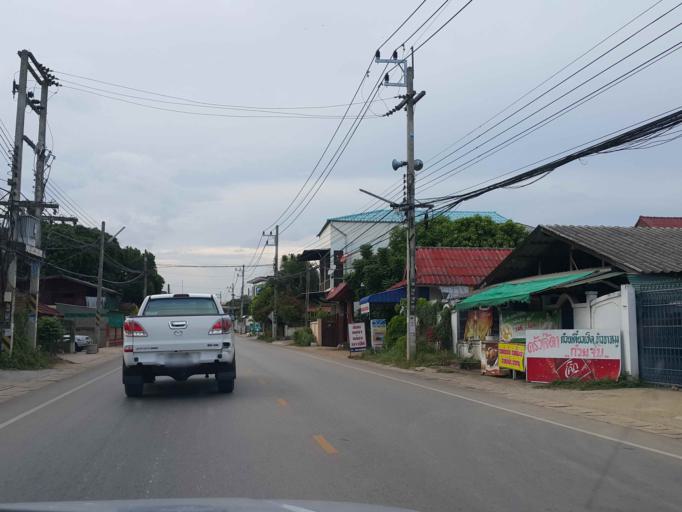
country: TH
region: Lampang
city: Ko Kha
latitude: 18.1919
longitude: 99.3943
